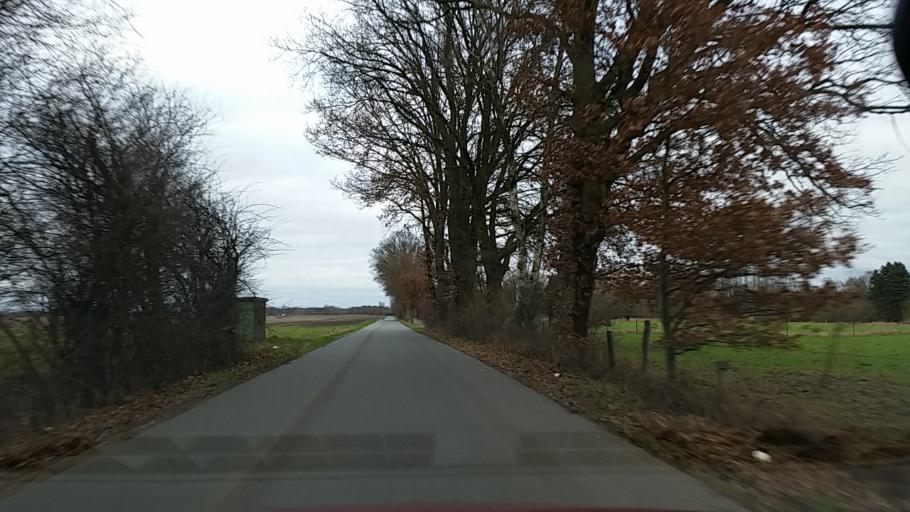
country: DE
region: Lower Saxony
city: Luder
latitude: 52.8143
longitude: 10.6677
